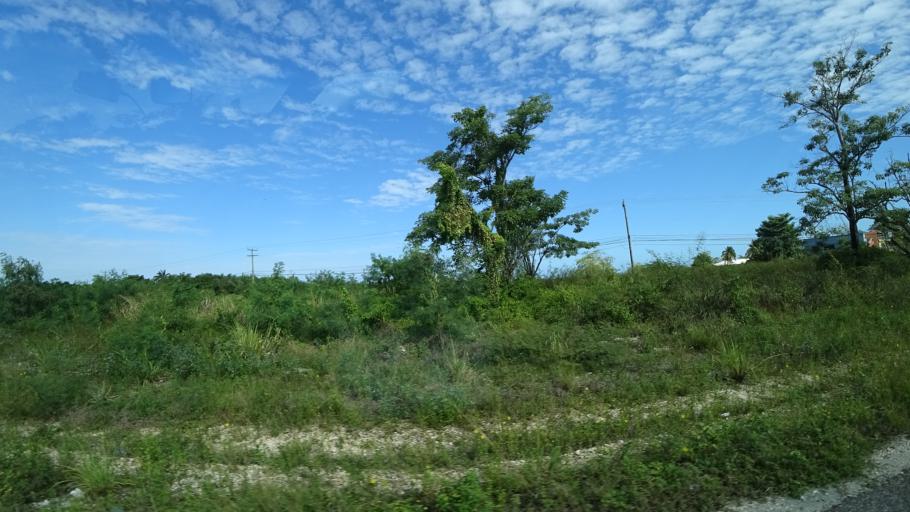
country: BZ
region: Belize
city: Belize City
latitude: 17.5428
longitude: -88.2620
